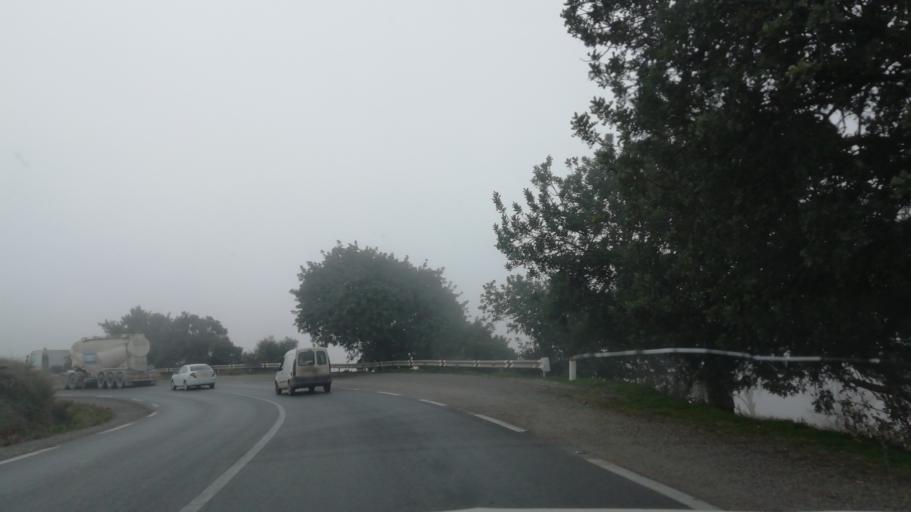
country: DZ
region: Mascara
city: Mascara
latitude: 35.5221
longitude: 0.3200
